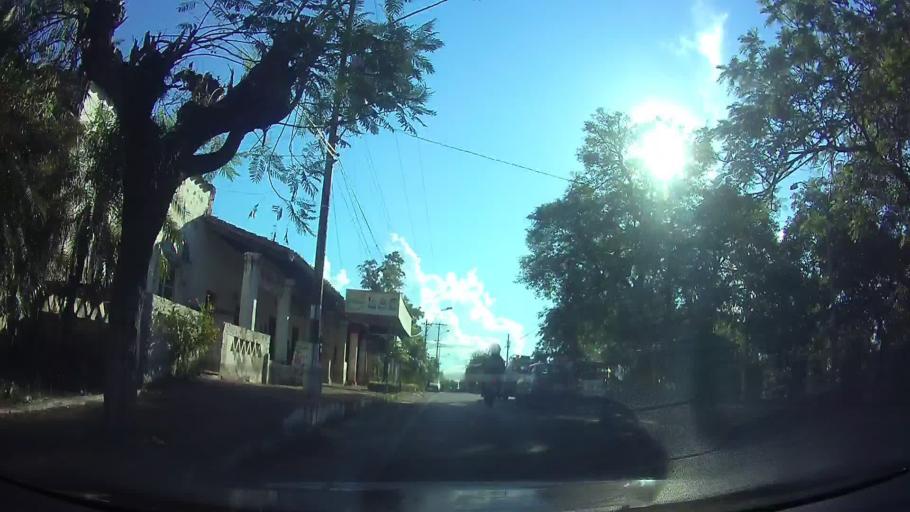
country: PY
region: Central
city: Aregua
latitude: -25.3139
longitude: -57.3854
